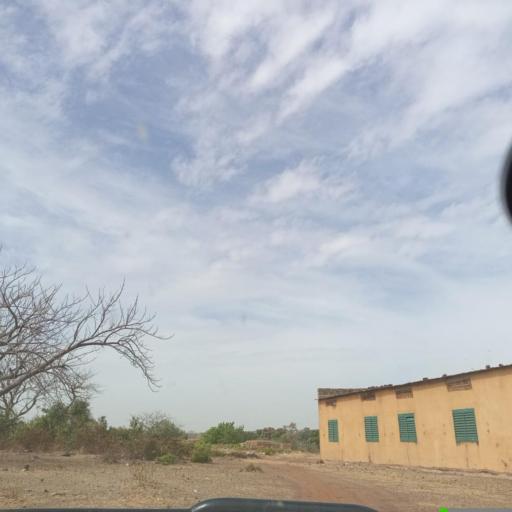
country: ML
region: Koulikoro
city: Koulikoro
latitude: 13.1653
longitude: -7.7277
